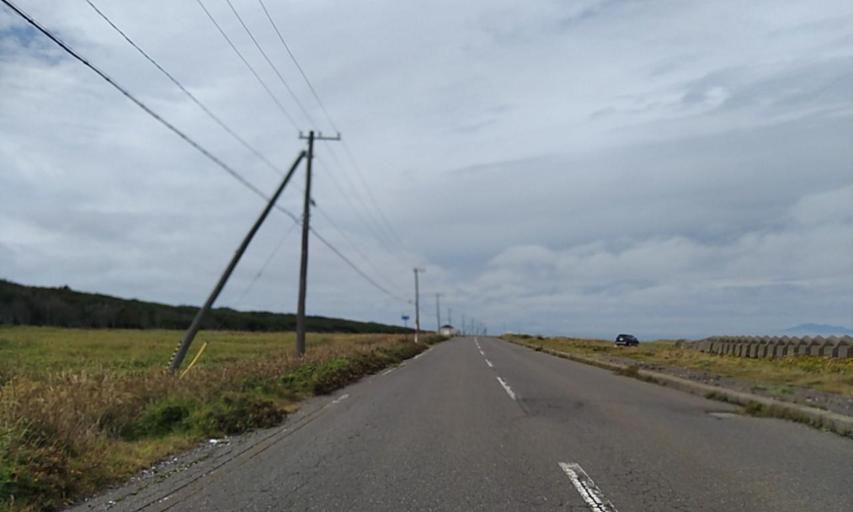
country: JP
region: Hokkaido
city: Shibetsu
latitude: 43.6065
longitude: 145.2901
